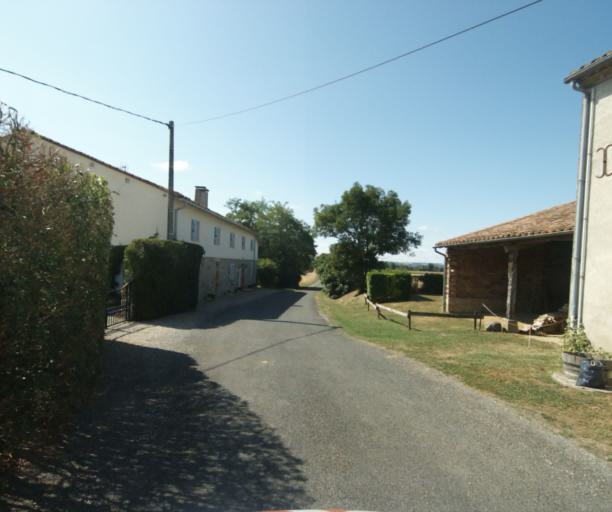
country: FR
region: Midi-Pyrenees
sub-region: Departement de la Haute-Garonne
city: Revel
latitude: 43.5042
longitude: 1.9747
